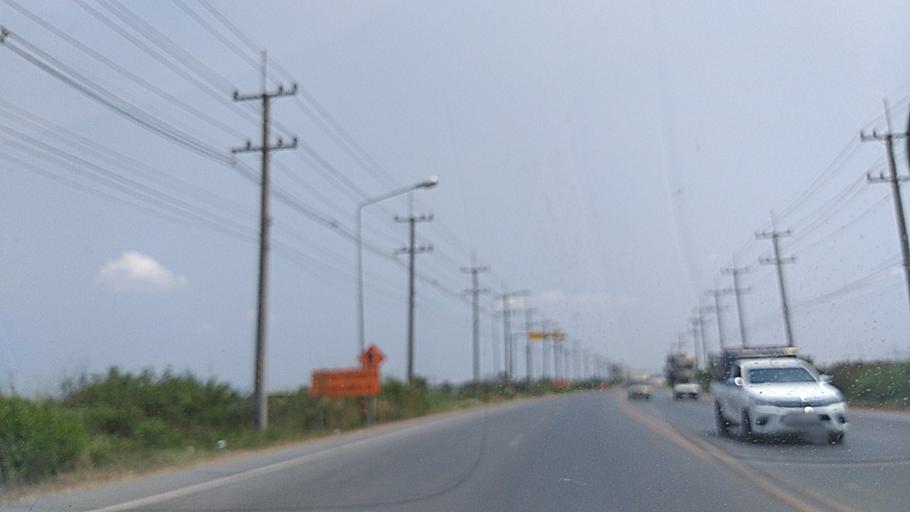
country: TH
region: Bangkok
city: Nong Chok
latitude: 13.9665
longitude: 100.9312
